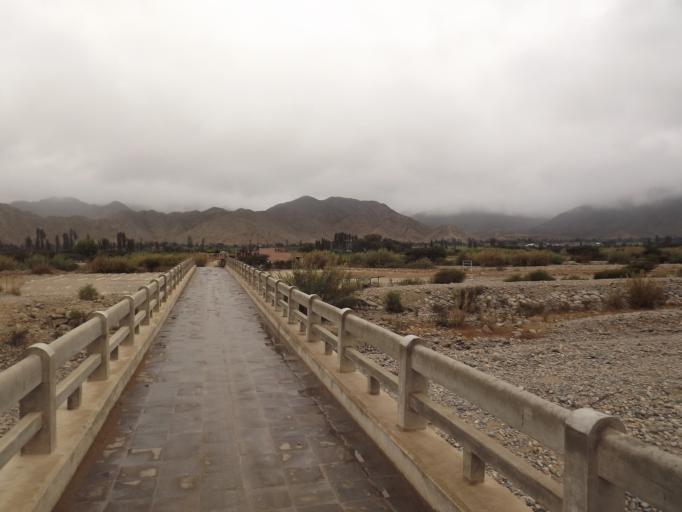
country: PE
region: Lima
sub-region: Huaura
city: Vegueta
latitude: -10.8938
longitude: -77.5112
